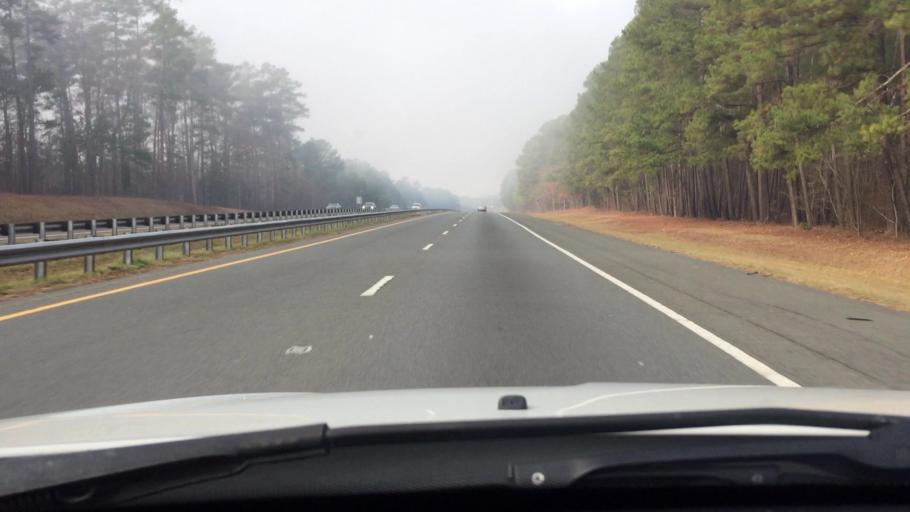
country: US
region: North Carolina
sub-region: Wake County
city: Holly Springs
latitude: 35.6442
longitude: -78.9915
